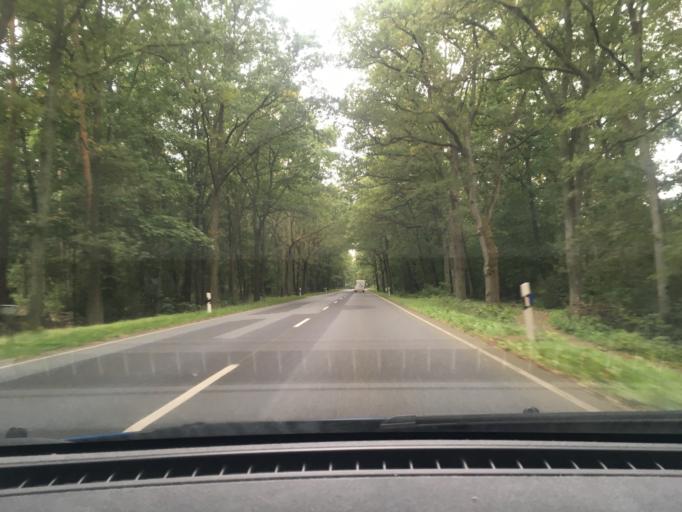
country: DE
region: Lower Saxony
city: Scharnhorst
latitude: 52.7557
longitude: 10.2758
